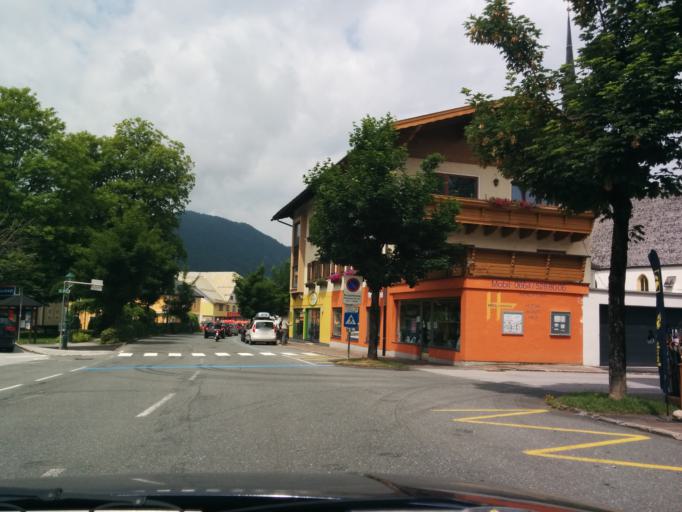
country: AT
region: Salzburg
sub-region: Politischer Bezirk Hallein
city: Abtenau
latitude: 47.5635
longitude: 13.3471
